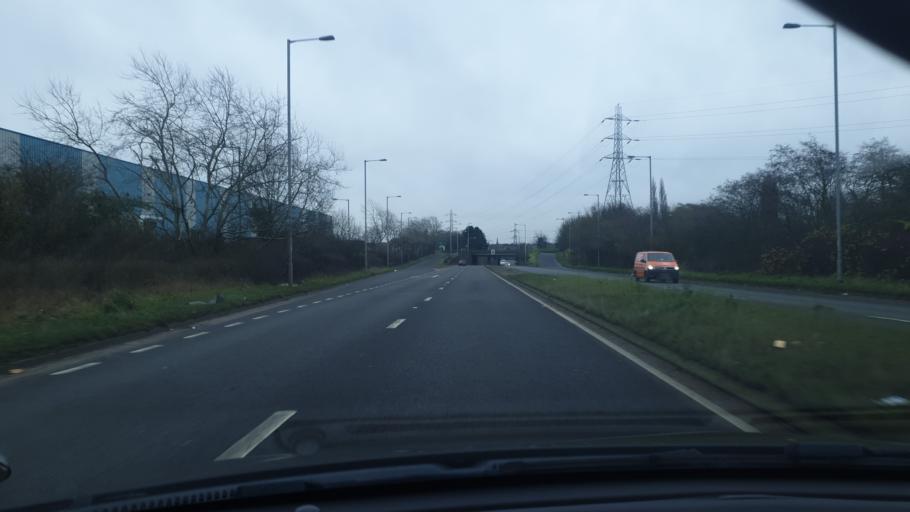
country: GB
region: England
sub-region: Walsall
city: Willenhall
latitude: 52.5789
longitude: -2.0595
